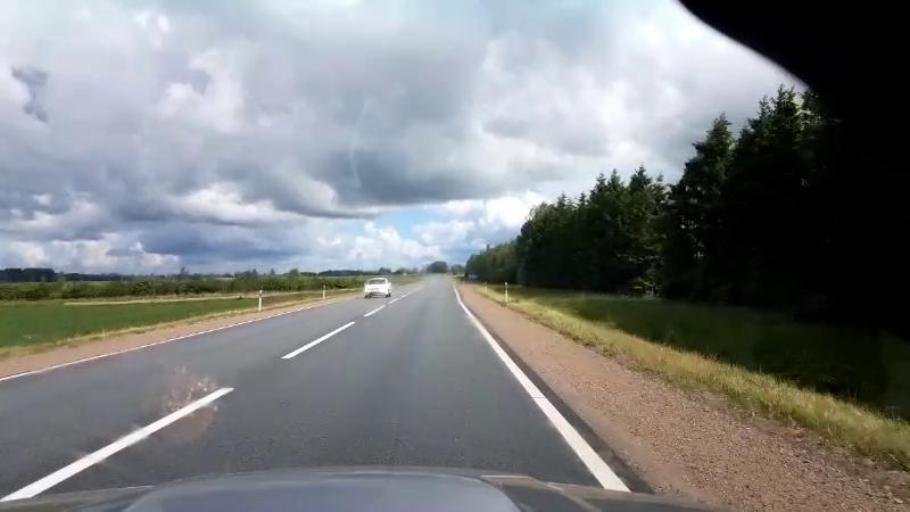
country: LV
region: Lecava
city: Iecava
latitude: 56.5333
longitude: 24.1714
